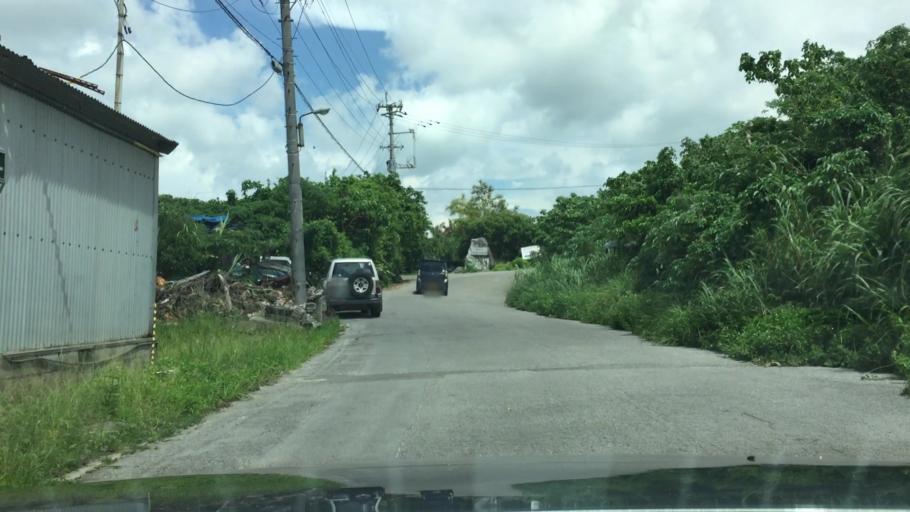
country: JP
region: Okinawa
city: Ishigaki
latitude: 24.3596
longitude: 124.1549
